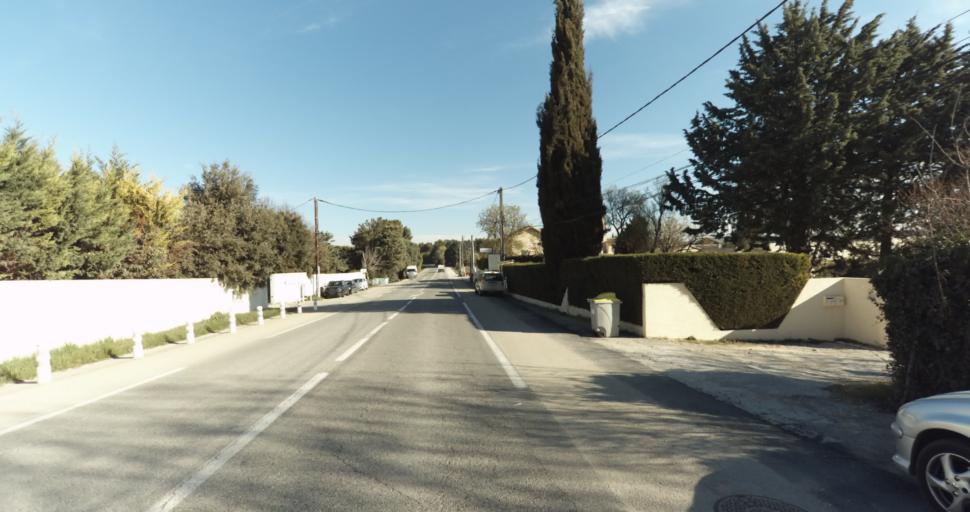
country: FR
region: Provence-Alpes-Cote d'Azur
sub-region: Departement des Bouches-du-Rhone
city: Aix-en-Provence
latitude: 43.5628
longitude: 5.4340
